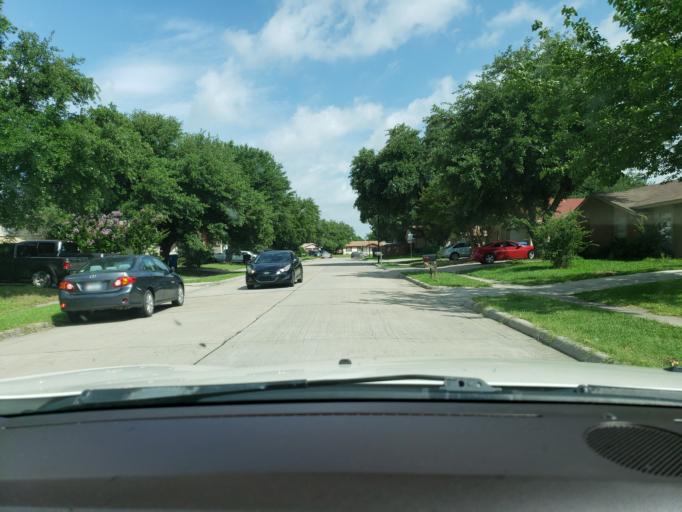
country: US
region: Texas
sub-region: Dallas County
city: Rowlett
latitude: 32.9138
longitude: -96.5762
